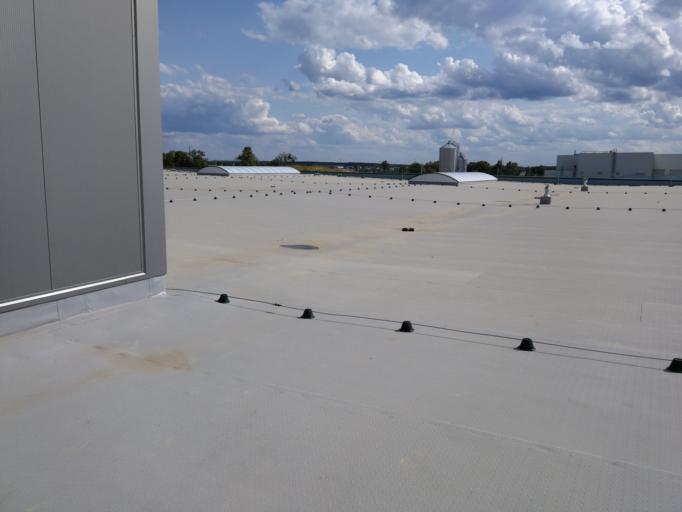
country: PL
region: Kujawsko-Pomorskie
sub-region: Powiat torunski
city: Lysomice
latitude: 53.1019
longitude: 18.6251
